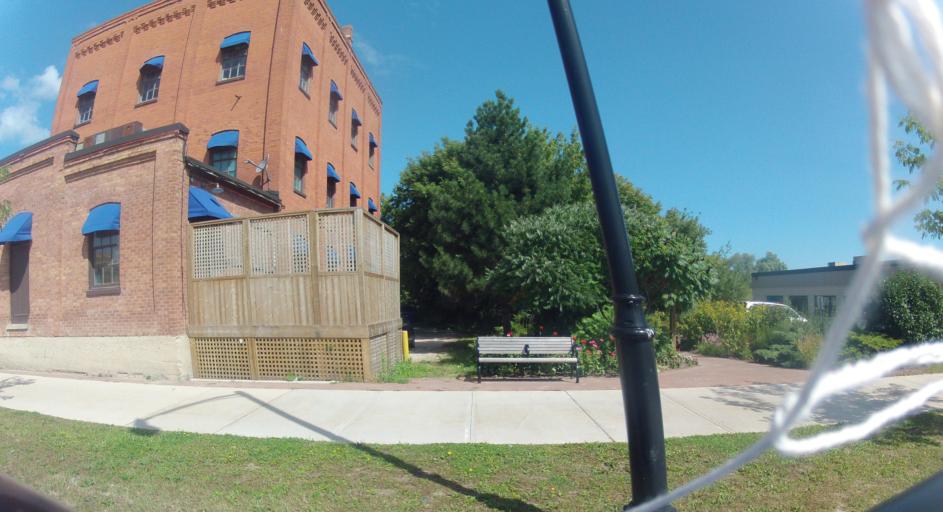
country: CA
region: Ontario
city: Collingwood
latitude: 44.5019
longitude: -80.2281
